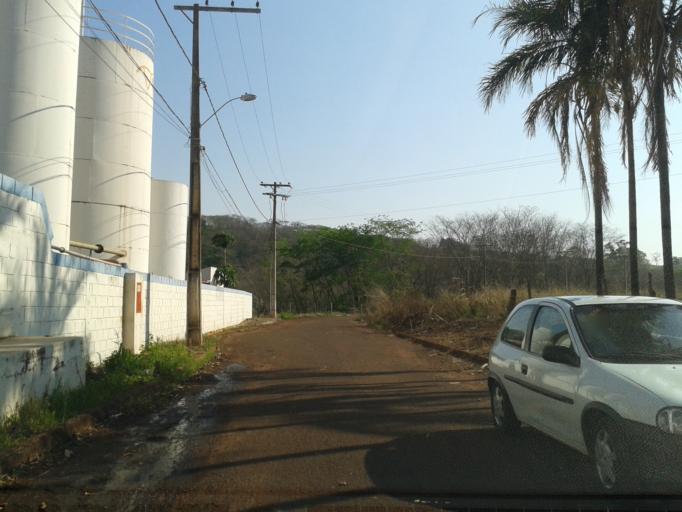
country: BR
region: Minas Gerais
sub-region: Ituiutaba
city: Ituiutaba
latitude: -18.9449
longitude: -49.4551
